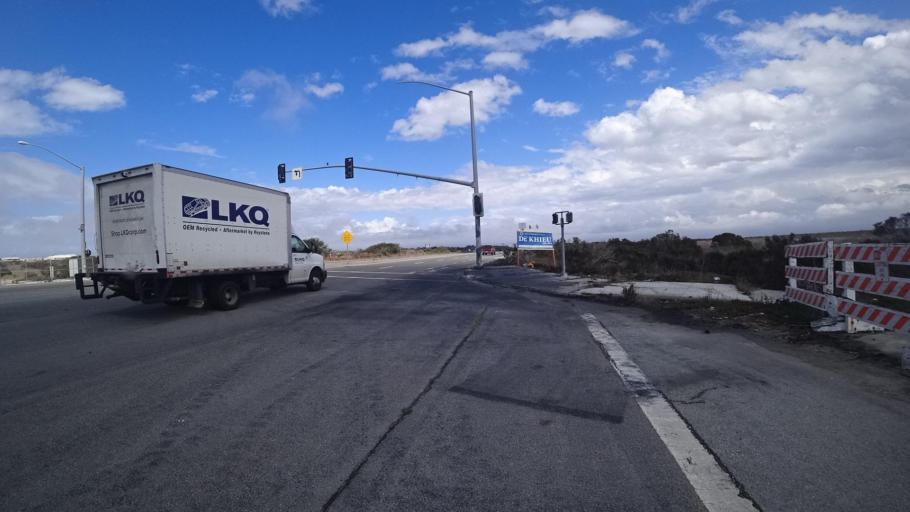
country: US
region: California
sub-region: Monterey County
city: Marina
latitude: 36.6679
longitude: -121.7539
